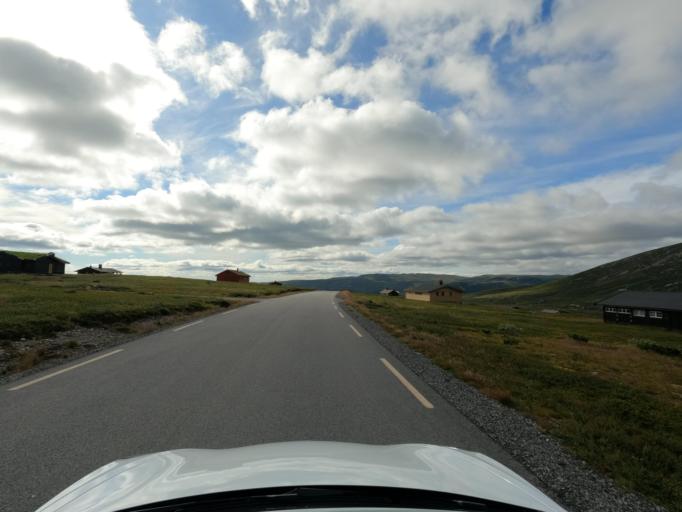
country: NO
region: Telemark
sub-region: Tinn
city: Rjukan
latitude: 60.1649
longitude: 8.6032
